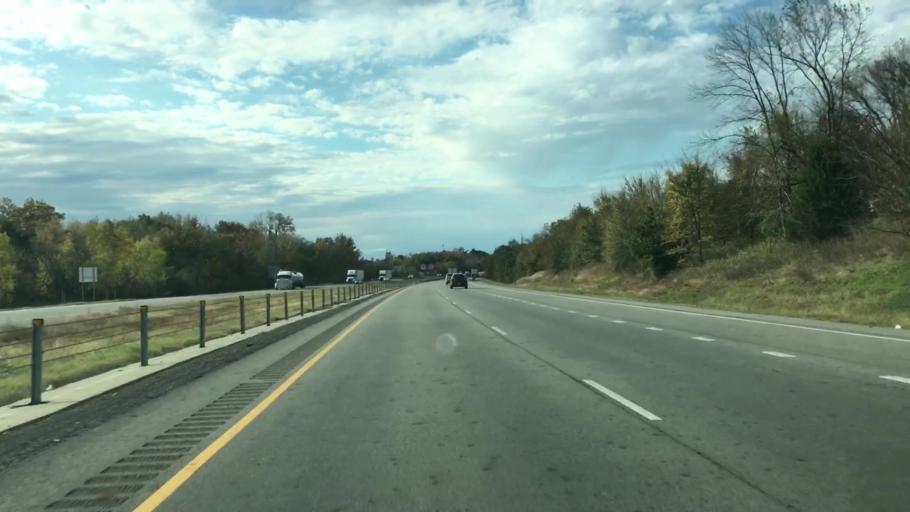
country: US
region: Arkansas
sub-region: Pope County
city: Pottsville
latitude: 35.2501
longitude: -93.0361
